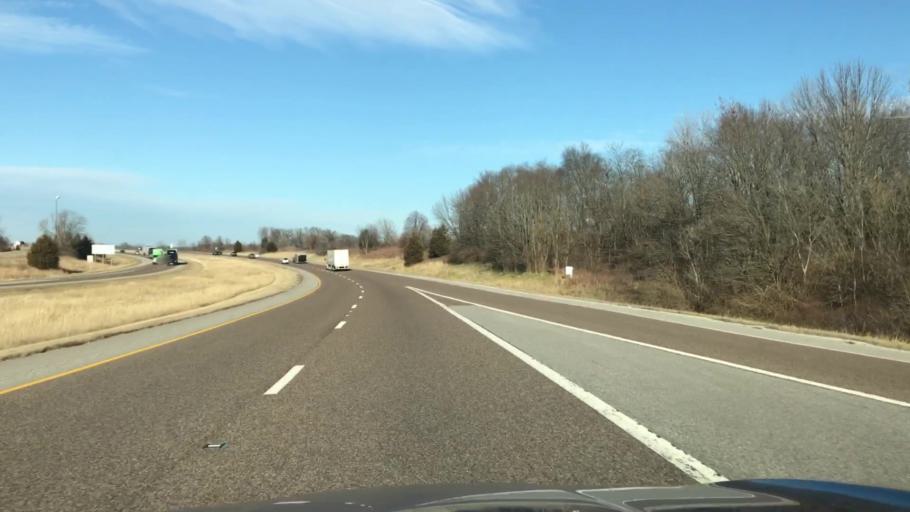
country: US
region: Illinois
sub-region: Macoupin County
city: Staunton
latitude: 38.9698
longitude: -89.7509
